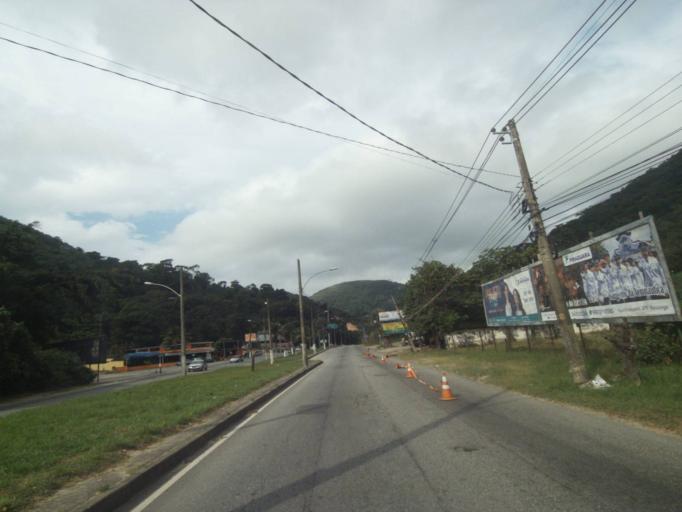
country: BR
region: Rio de Janeiro
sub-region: Nilopolis
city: Nilopolis
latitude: -22.8991
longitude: -43.3907
